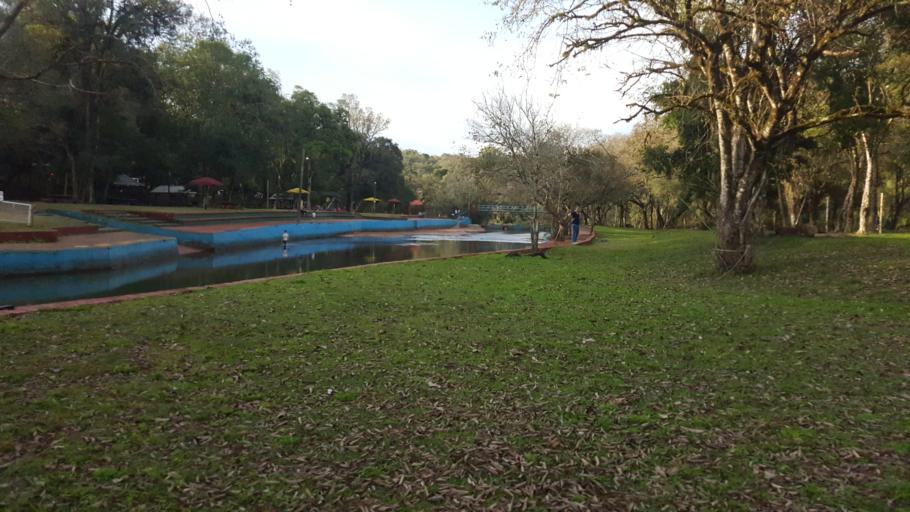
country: AR
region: Misiones
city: Puerto Leoni
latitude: -27.0017
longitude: -55.1790
